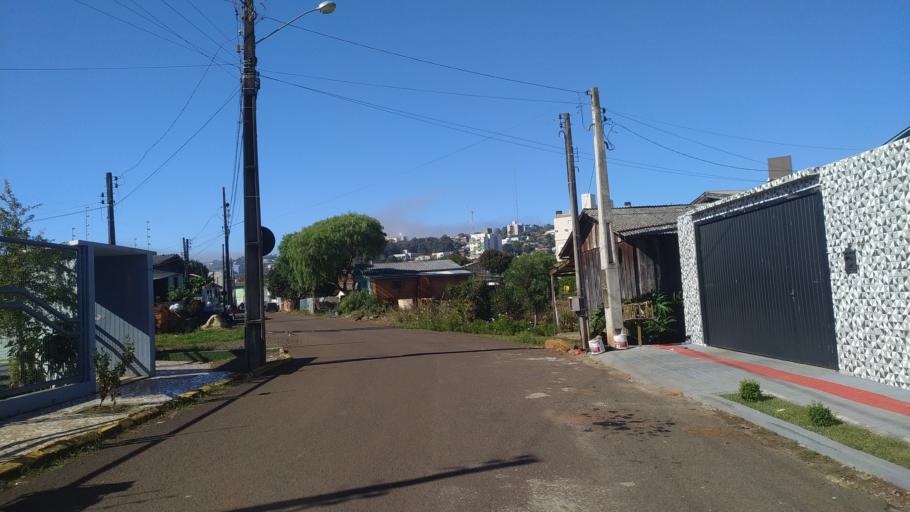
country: BR
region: Santa Catarina
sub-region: Chapeco
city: Chapeco
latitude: -27.1133
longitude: -52.6013
